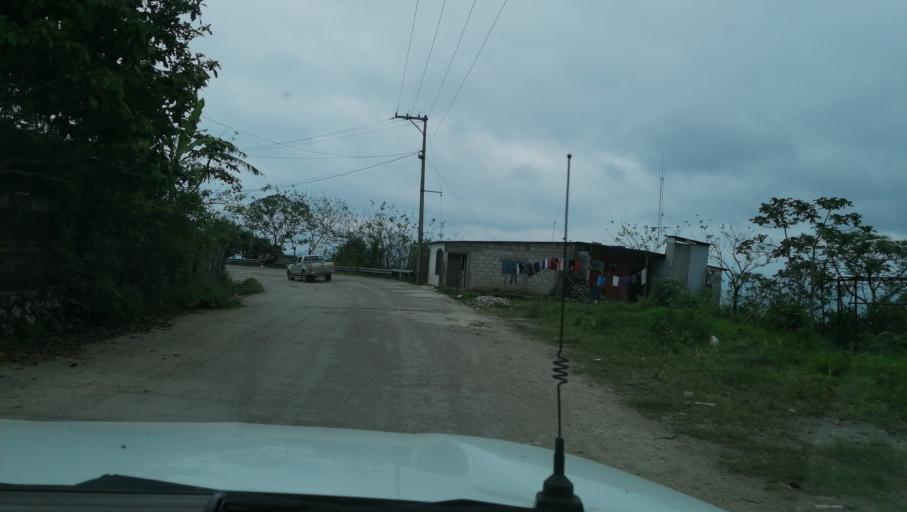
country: MX
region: Chiapas
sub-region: Francisco Leon
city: San Miguel la Sardina
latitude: 17.2852
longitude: -93.2737
